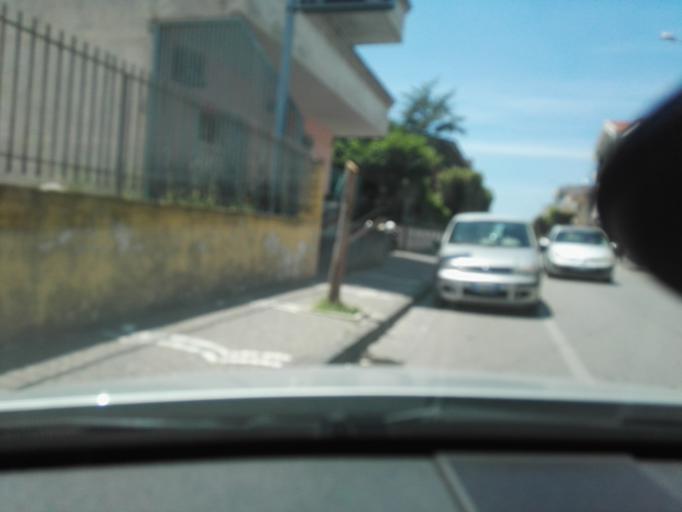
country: IT
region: Campania
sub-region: Provincia di Caserta
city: Casapesenna
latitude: 40.9917
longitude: 14.1343
